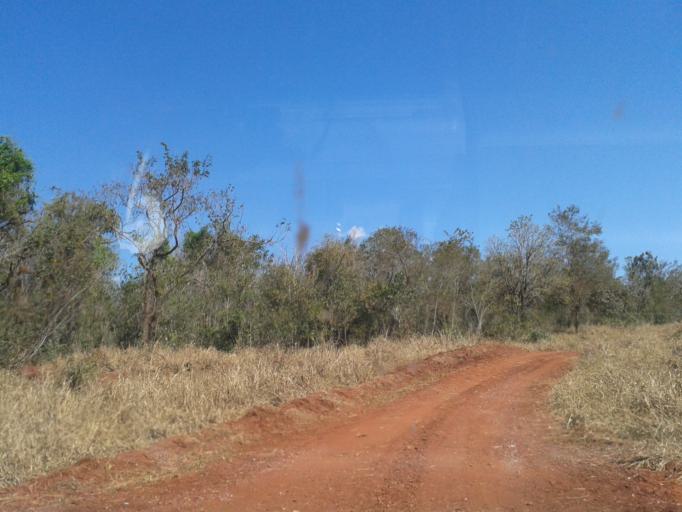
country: BR
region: Minas Gerais
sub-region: Santa Vitoria
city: Santa Vitoria
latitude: -19.0169
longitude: -50.4476
